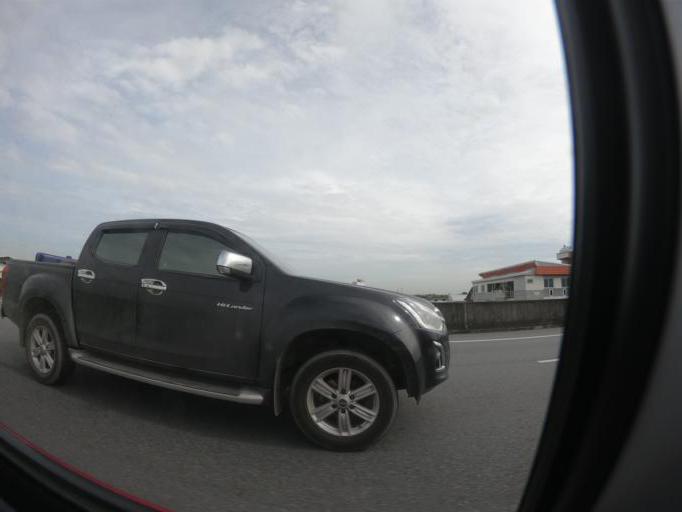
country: TH
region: Bangkok
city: Sai Mai
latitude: 13.8969
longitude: 100.6711
